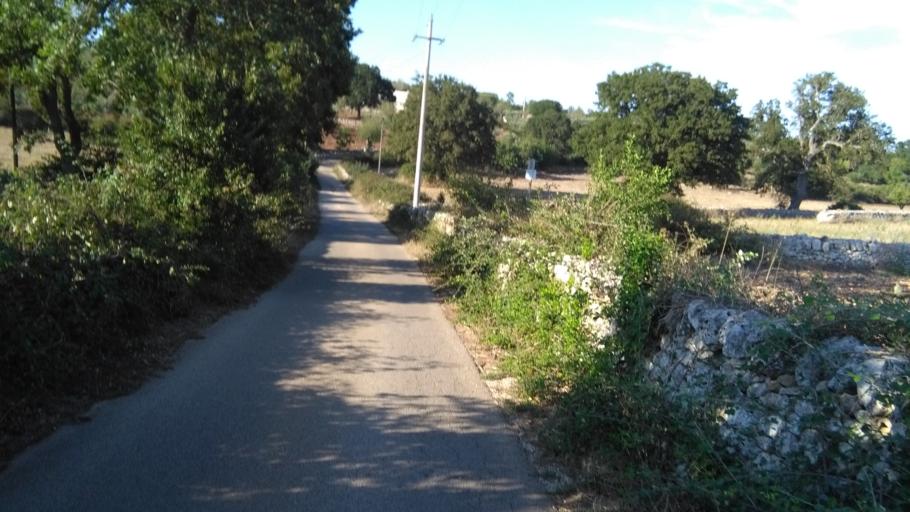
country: IT
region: Apulia
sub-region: Provincia di Bari
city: Putignano
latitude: 40.8288
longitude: 17.0590
